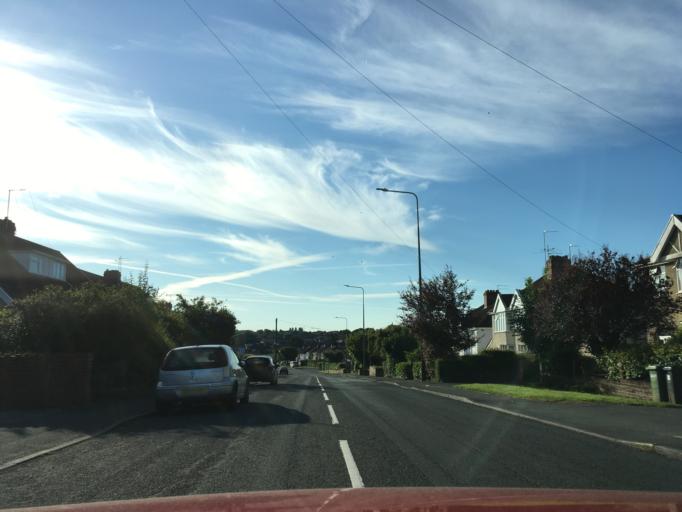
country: GB
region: England
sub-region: South Gloucestershire
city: Mangotsfield
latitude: 51.4886
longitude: -2.4975
